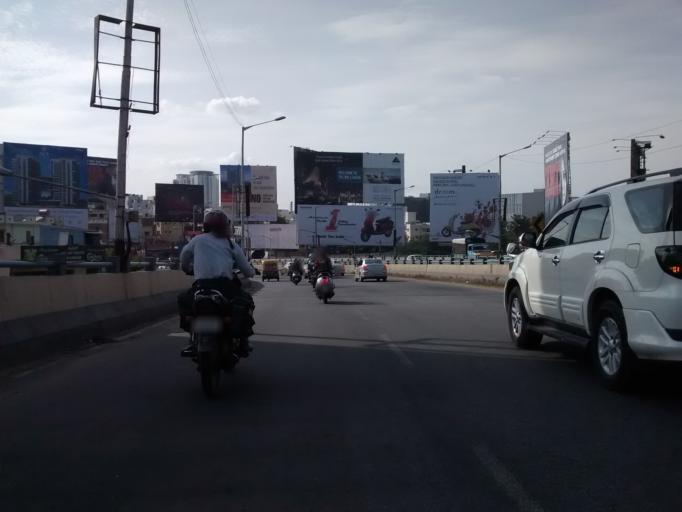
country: IN
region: Karnataka
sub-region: Bangalore Urban
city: Yelahanka
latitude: 13.0403
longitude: 77.6241
